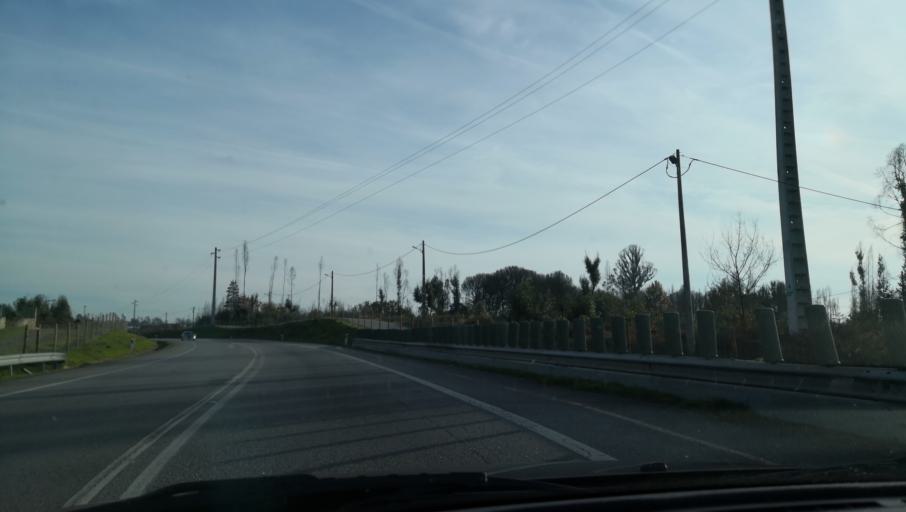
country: PT
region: Viseu
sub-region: Concelho de Tondela
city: Tondela
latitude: 40.5164
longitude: -8.0935
